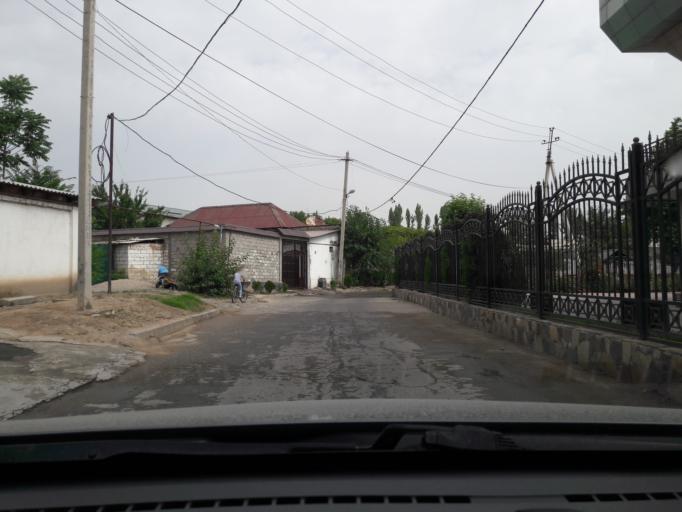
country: TJ
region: Dushanbe
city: Dushanbe
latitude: 38.5800
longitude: 68.7645
